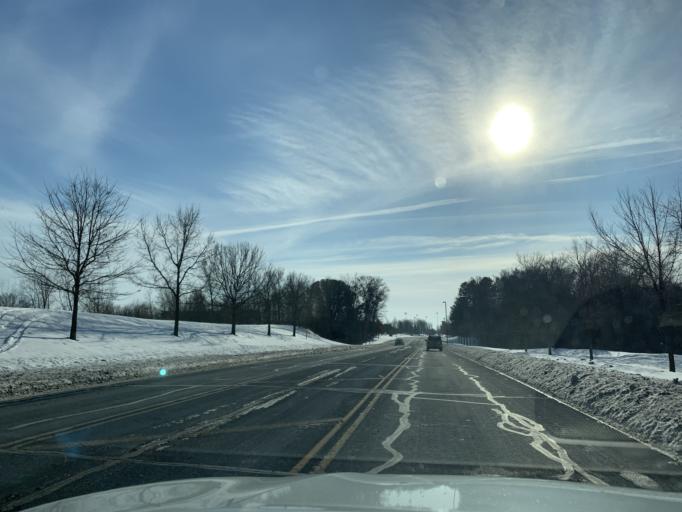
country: US
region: Minnesota
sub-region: Anoka County
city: Columbus
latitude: 45.2486
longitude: -93.0349
